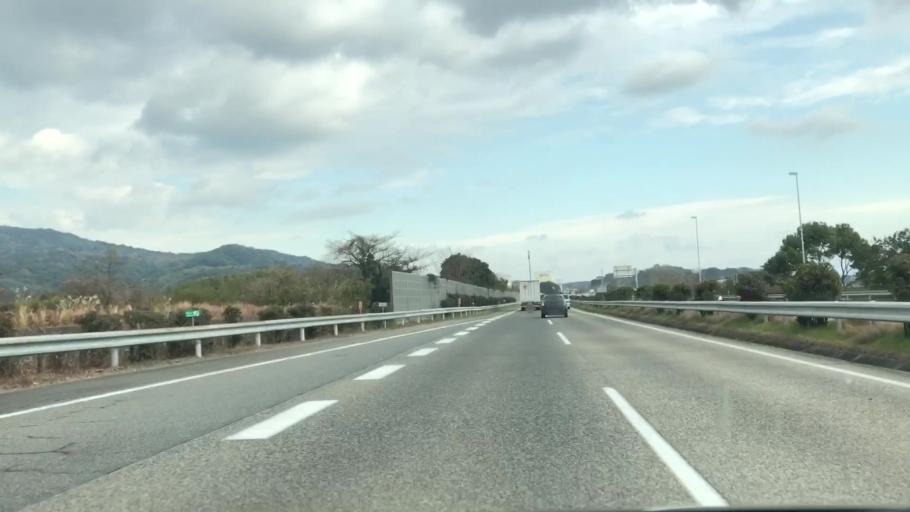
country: JP
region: Saga Prefecture
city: Kanzakimachi-kanzaki
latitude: 33.3542
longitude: 130.3975
